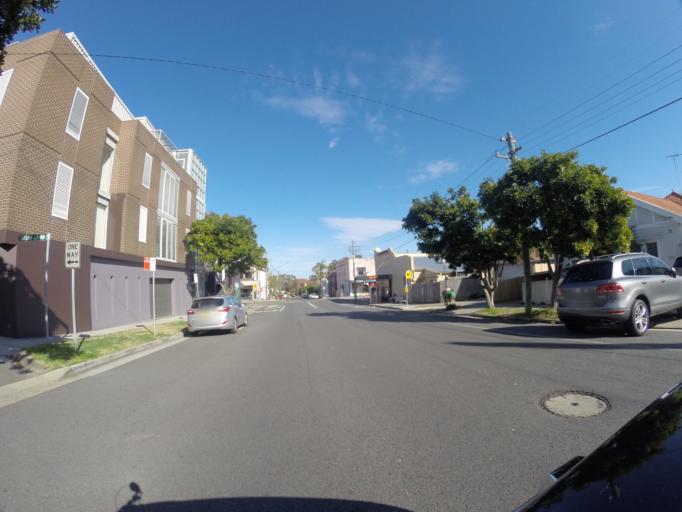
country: AU
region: New South Wales
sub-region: Randwick
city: Clovelly
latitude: -33.9110
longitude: 151.2544
